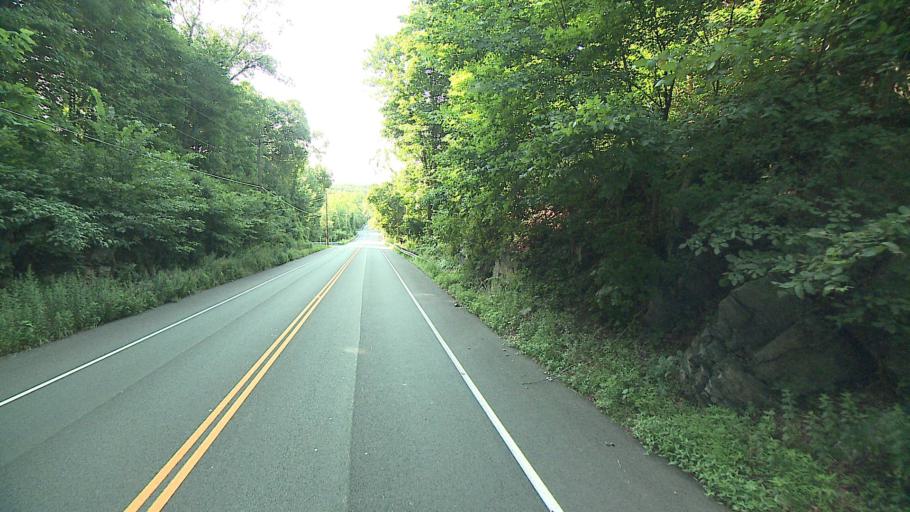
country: US
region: Connecticut
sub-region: Fairfield County
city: Ridgefield
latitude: 41.3095
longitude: -73.4680
